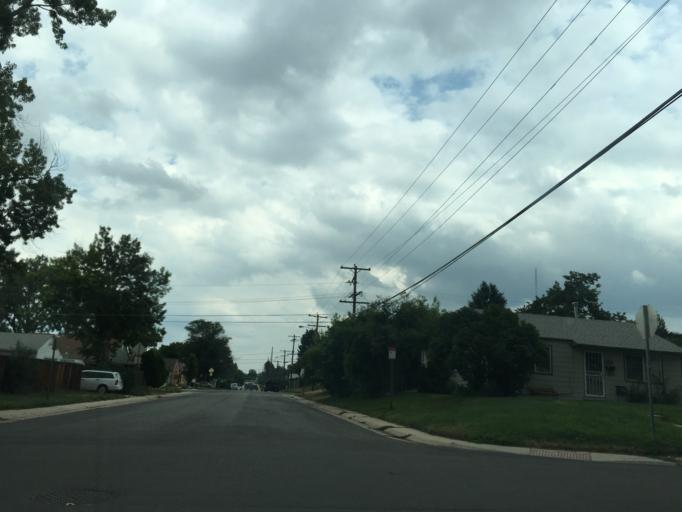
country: US
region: Colorado
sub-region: Arapahoe County
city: Sheridan
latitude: 39.6859
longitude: -105.0141
